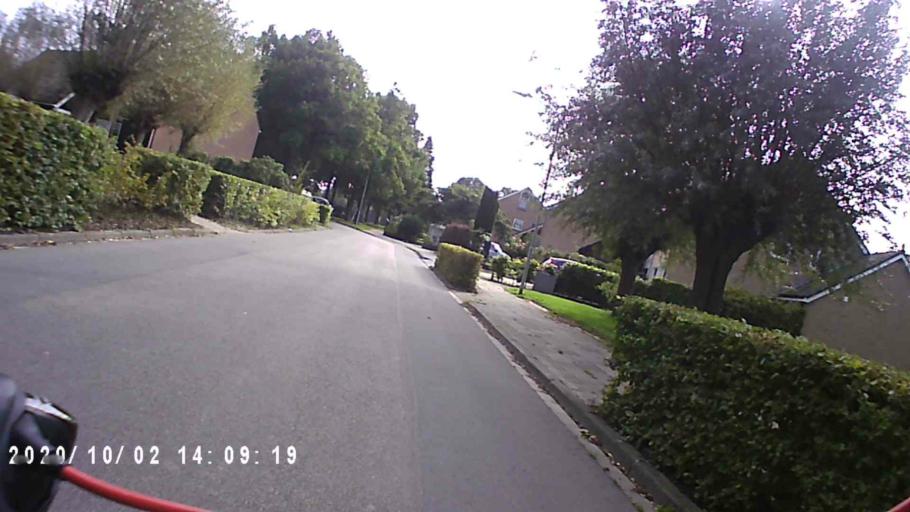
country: NL
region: Groningen
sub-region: Gemeente Zuidhorn
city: Zuidhorn
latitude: 53.2474
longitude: 6.3986
